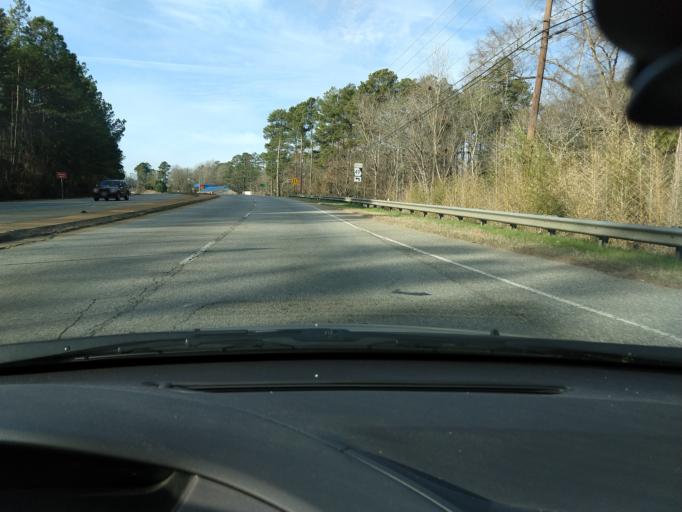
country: US
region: Georgia
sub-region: Sumter County
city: Americus
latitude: 32.0614
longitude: -84.2666
